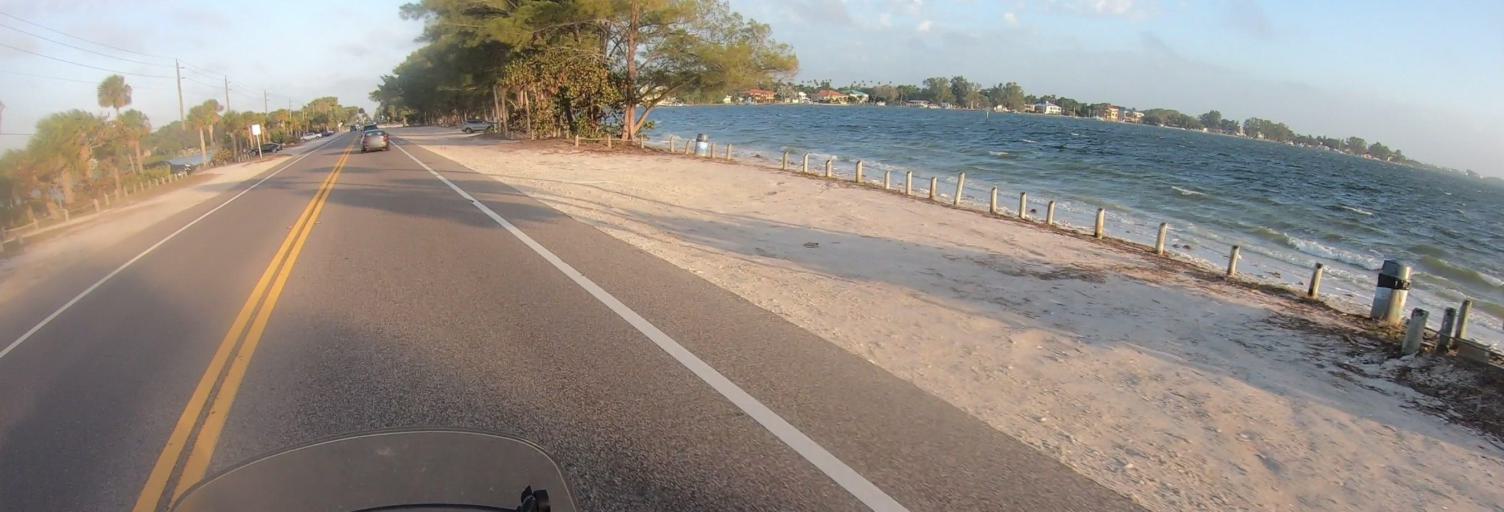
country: US
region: Florida
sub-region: Manatee County
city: West Bradenton
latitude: 27.4973
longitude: -82.6500
